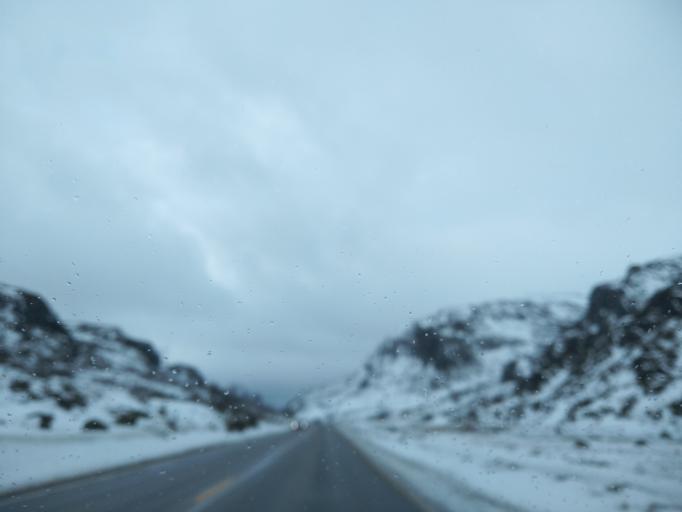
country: NO
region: Vest-Agder
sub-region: Sirdal
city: Tonstad
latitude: 58.9051
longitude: 6.7090
